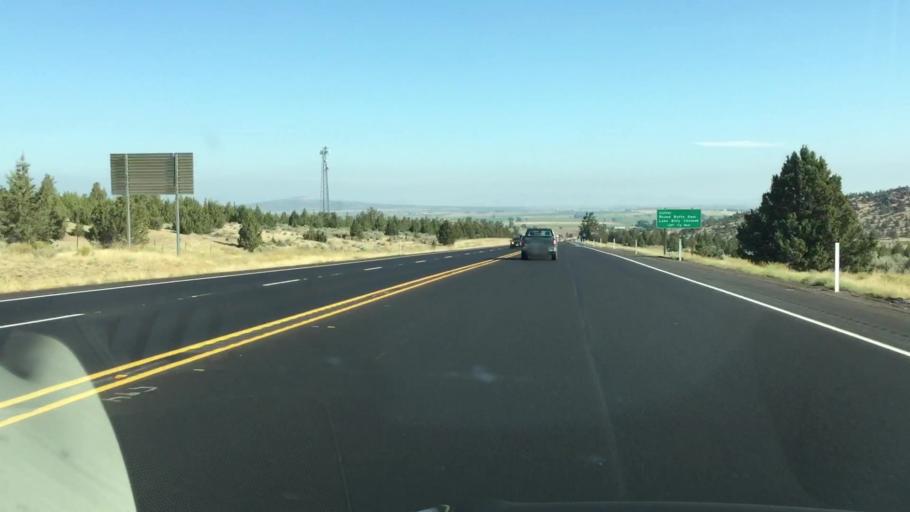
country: US
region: Oregon
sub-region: Jefferson County
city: Culver
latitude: 44.4825
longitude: -121.1941
